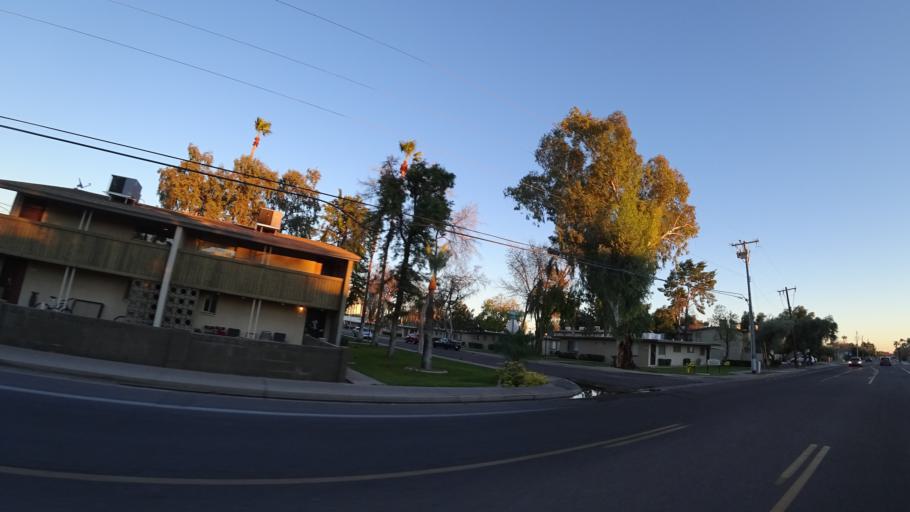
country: US
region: Arizona
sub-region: Maricopa County
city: Tempe Junction
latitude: 33.4265
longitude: -111.9523
